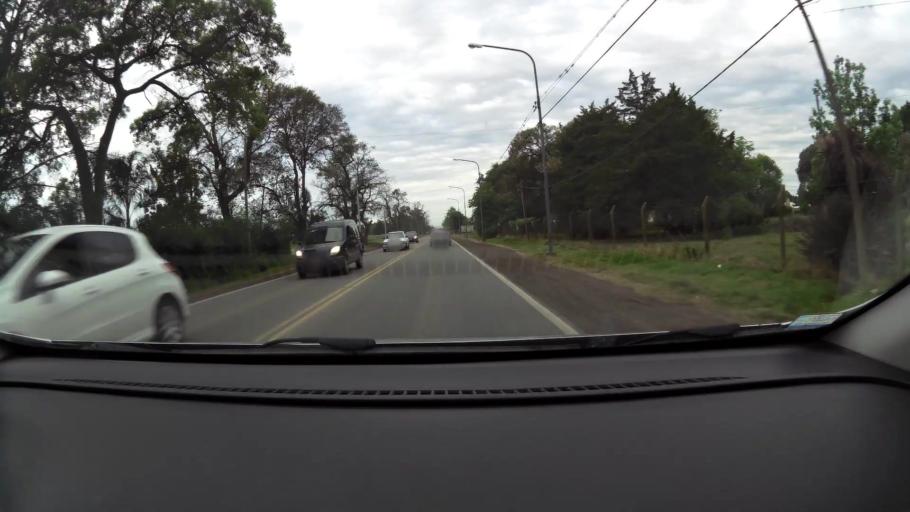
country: AR
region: Buenos Aires
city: San Nicolas de los Arroyos
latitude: -33.3778
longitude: -60.2087
